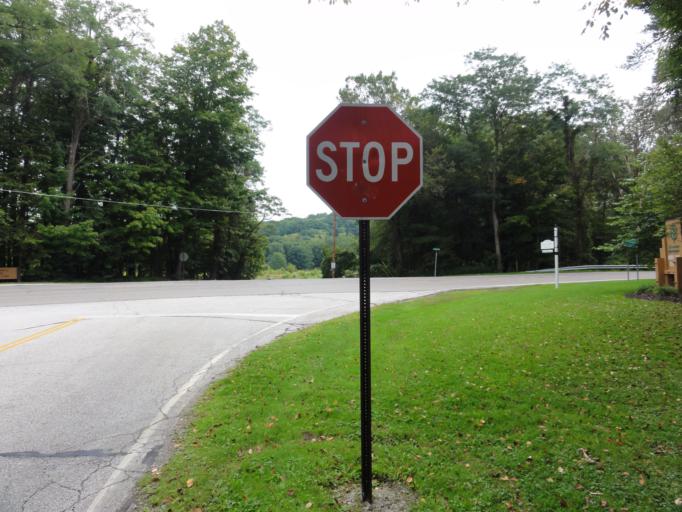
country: US
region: Ohio
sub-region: Cuyahoga County
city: Mayfield
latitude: 41.5695
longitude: -81.4180
